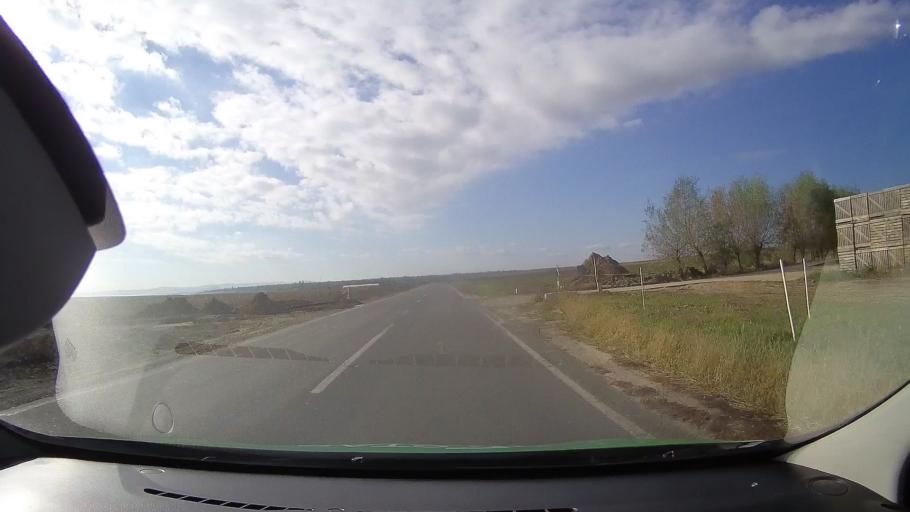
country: RO
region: Tulcea
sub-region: Comuna Sarichioi
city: Sarichioi
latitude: 44.9677
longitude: 28.8673
